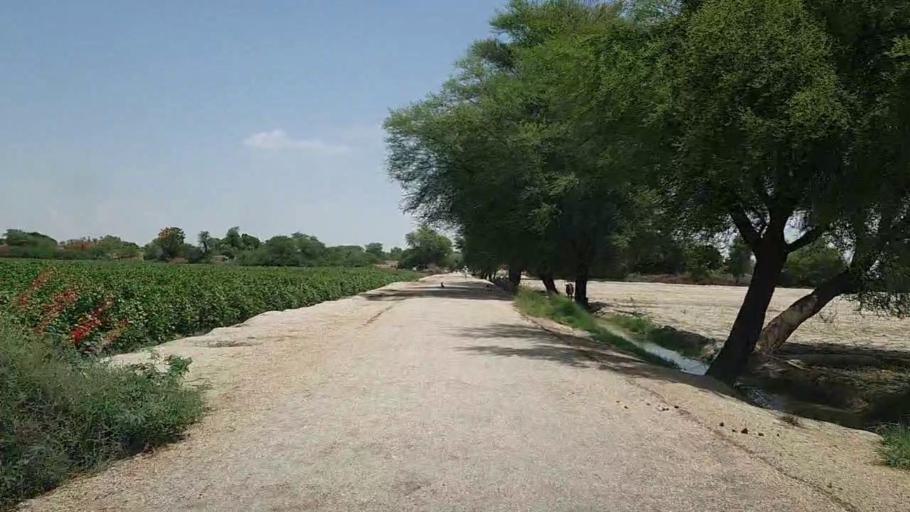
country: PK
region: Sindh
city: Pad Idan
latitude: 26.7444
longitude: 68.3057
